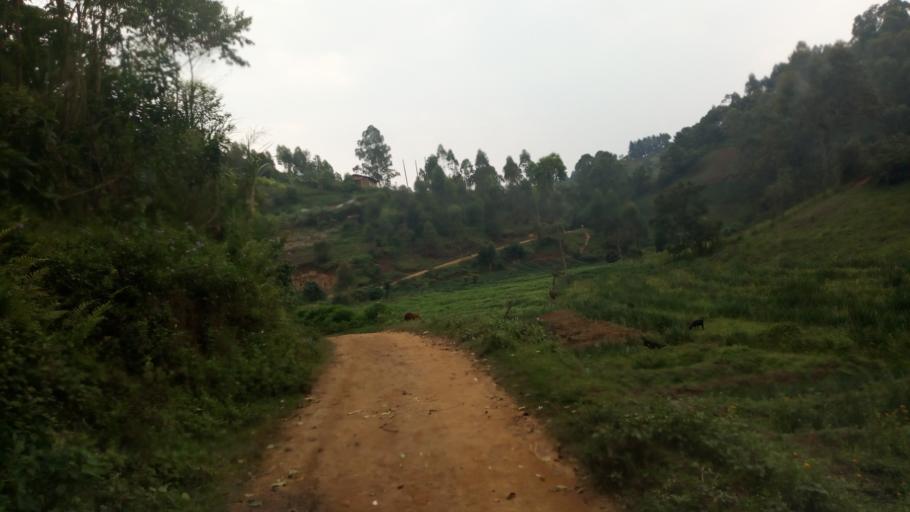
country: UG
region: Western Region
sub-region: Kisoro District
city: Kisoro
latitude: -1.2537
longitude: 29.6295
